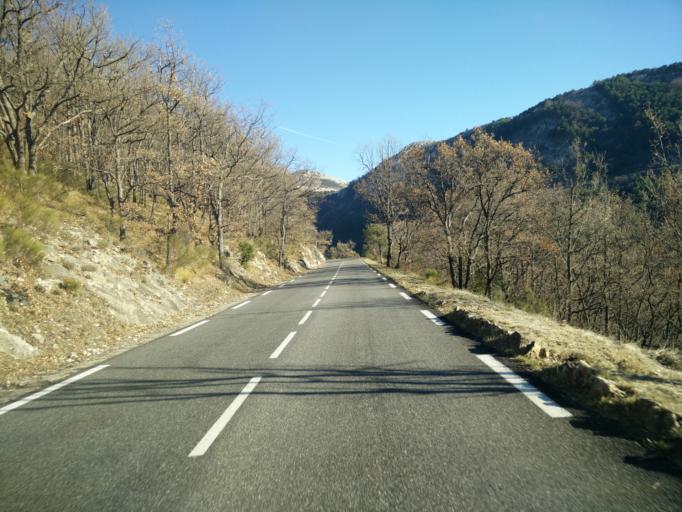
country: FR
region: Provence-Alpes-Cote d'Azur
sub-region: Departement des Alpes-Maritimes
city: Saint-Vallier-de-Thiey
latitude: 43.7169
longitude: 6.8443
